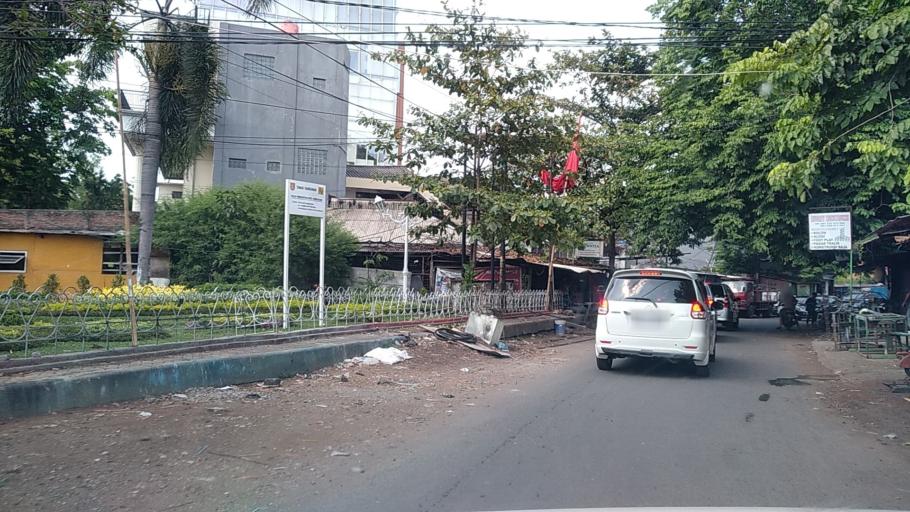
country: ID
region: Central Java
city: Semarang
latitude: -6.9890
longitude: 110.4297
